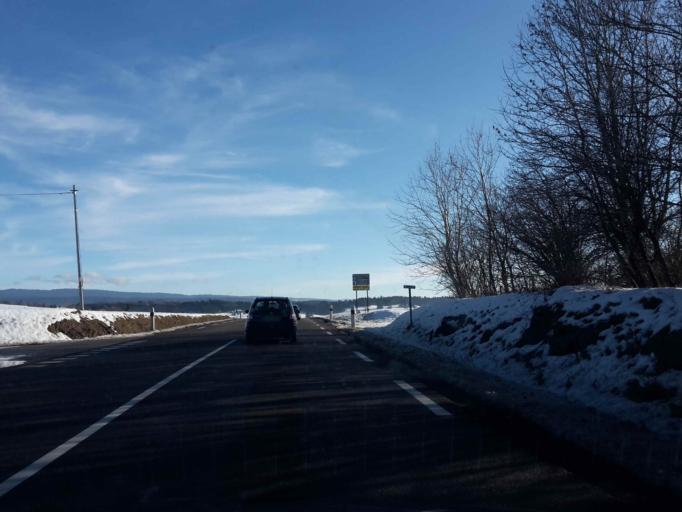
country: FR
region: Franche-Comte
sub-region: Departement du Doubs
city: Doubs
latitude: 46.9875
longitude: 6.3294
